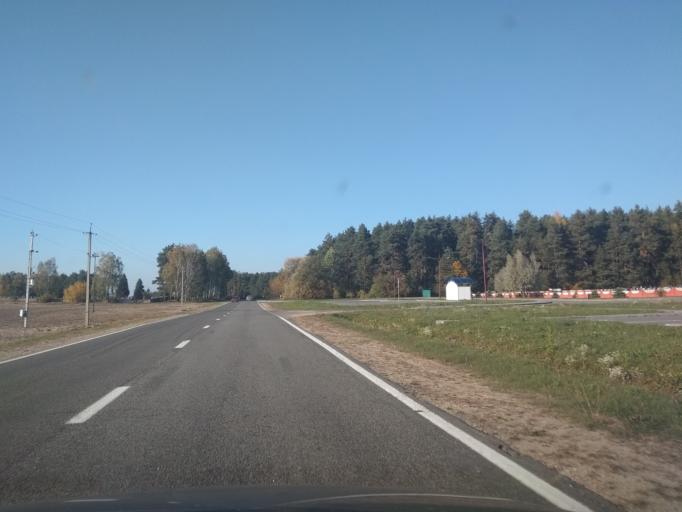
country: BY
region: Grodnenskaya
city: Vawkavysk
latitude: 53.1507
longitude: 24.4996
